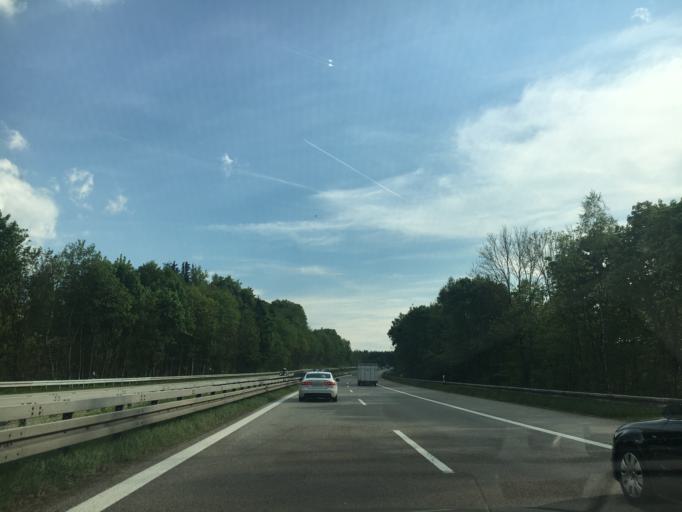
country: DE
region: Bavaria
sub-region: Upper Bavaria
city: Icking
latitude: 47.9459
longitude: 11.4095
